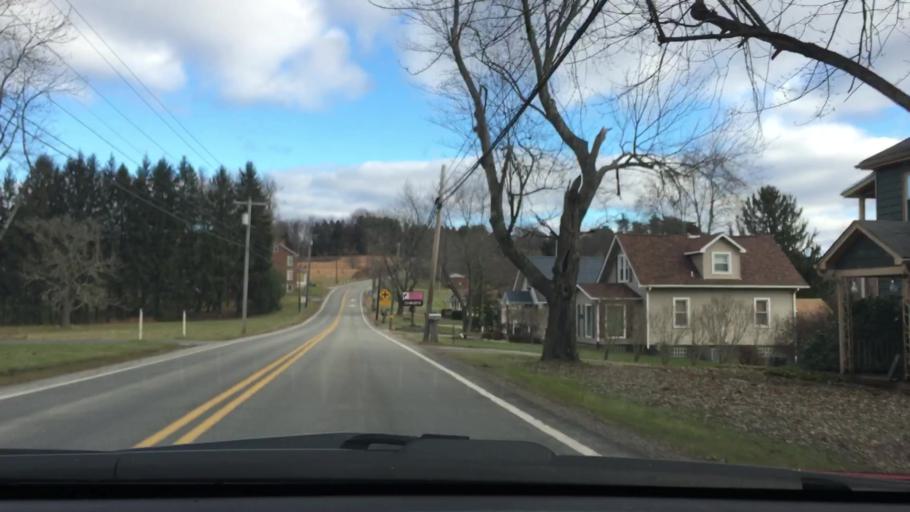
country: US
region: Pennsylvania
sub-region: Armstrong County
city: Orchard Hills
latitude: 40.5948
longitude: -79.5168
